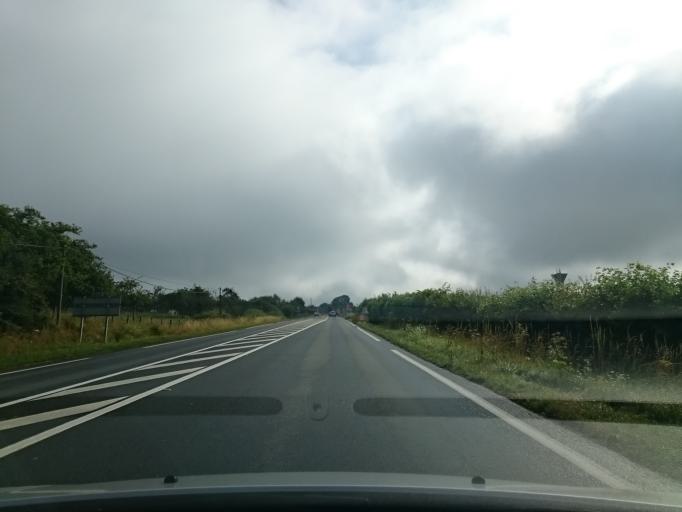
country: FR
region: Lower Normandy
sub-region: Departement du Calvados
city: Cambremer
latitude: 49.1350
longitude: 0.1249
